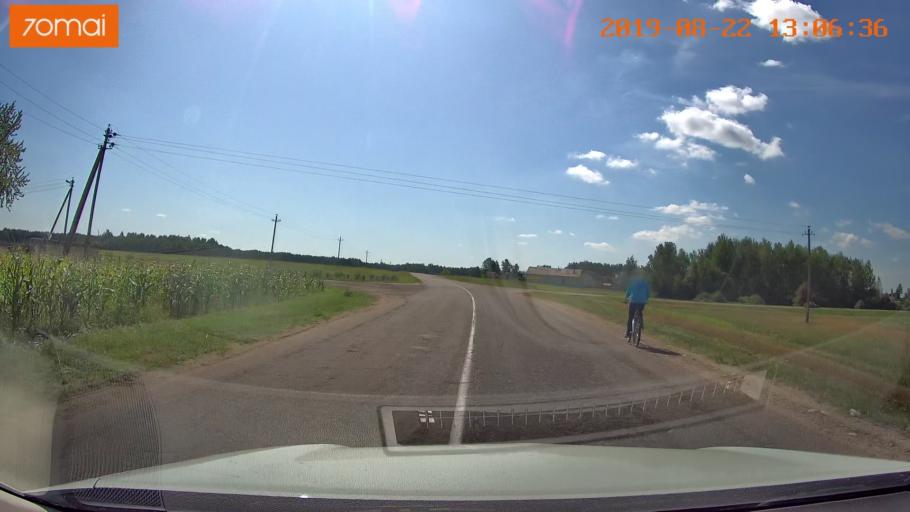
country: BY
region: Minsk
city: Prawdzinski
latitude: 53.3454
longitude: 27.8373
